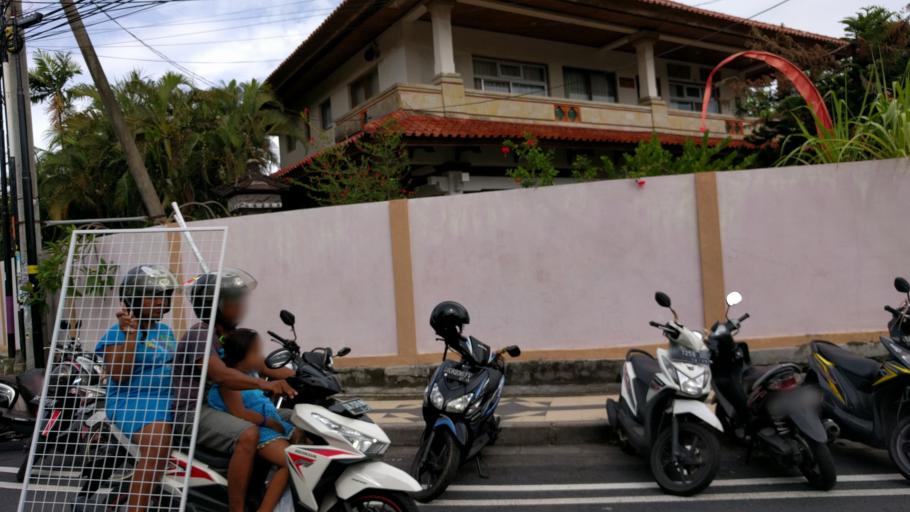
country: ID
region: Bali
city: Kuta
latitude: -8.6916
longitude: 115.1636
